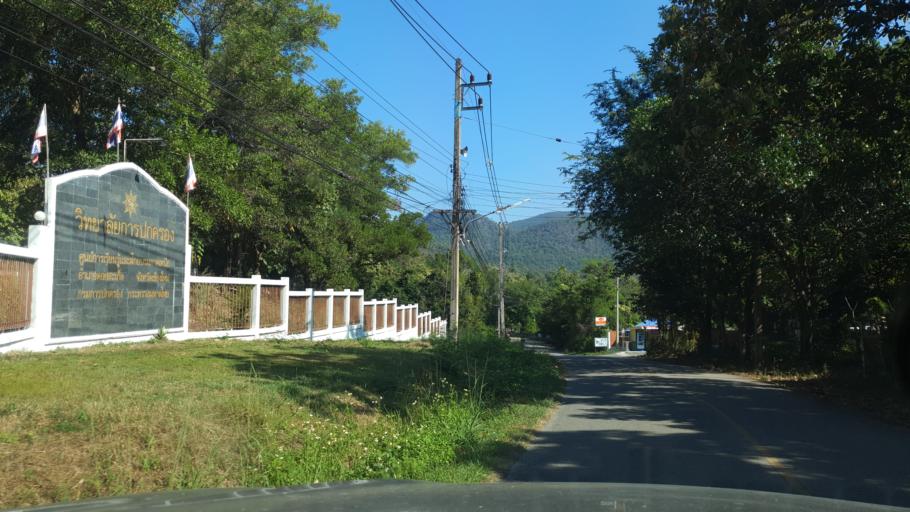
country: TH
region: Chiang Mai
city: San Sai
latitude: 18.8854
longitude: 99.1644
